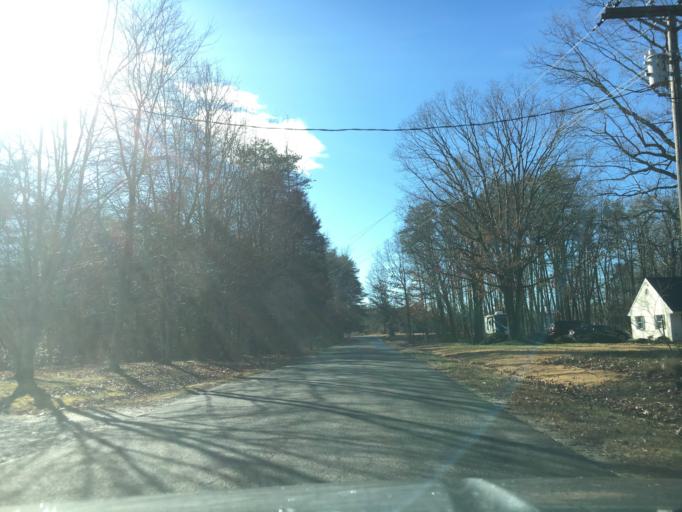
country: US
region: Virginia
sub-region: Fauquier County
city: Bealeton
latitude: 38.4555
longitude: -77.6516
